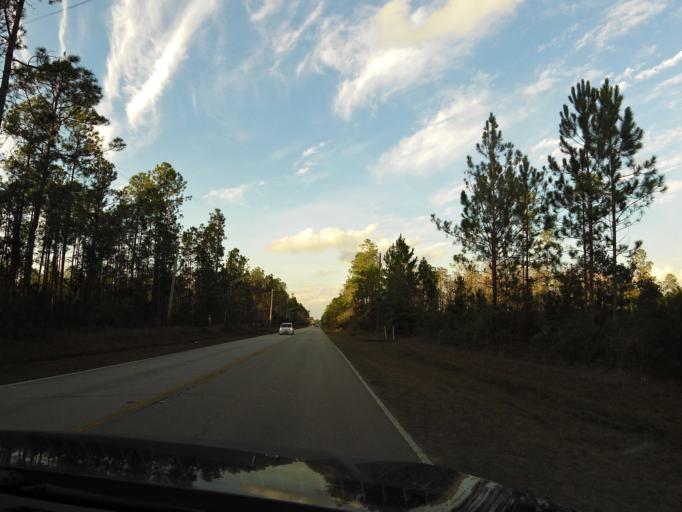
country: US
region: Florida
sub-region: Duval County
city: Baldwin
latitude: 30.1876
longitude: -81.9910
